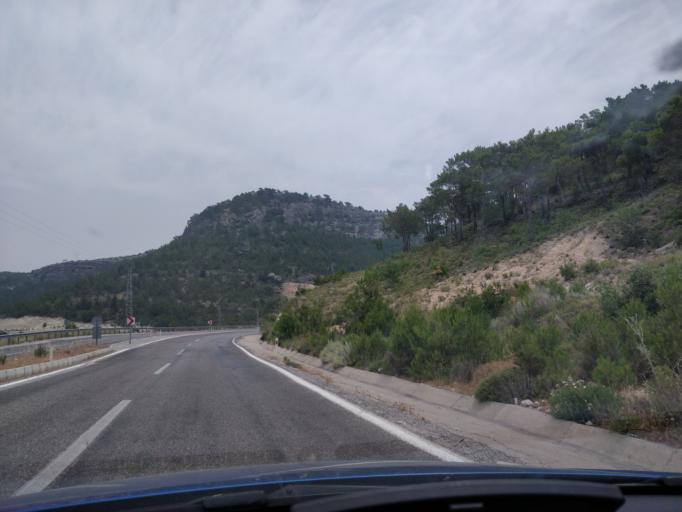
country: TR
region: Mersin
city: Tasucu
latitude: 36.3985
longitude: 33.8484
